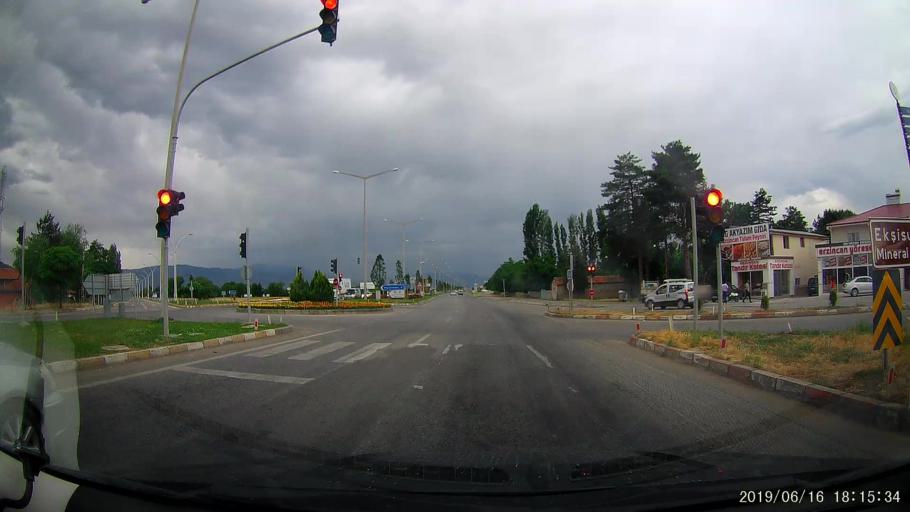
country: TR
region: Erzincan
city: Erzincan
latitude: 39.7265
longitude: 39.5529
